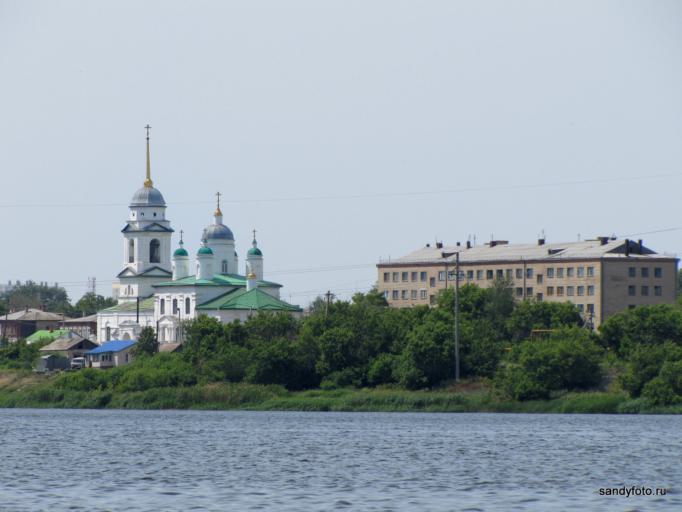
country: RU
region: Chelyabinsk
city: Troitsk
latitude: 54.0794
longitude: 61.5780
